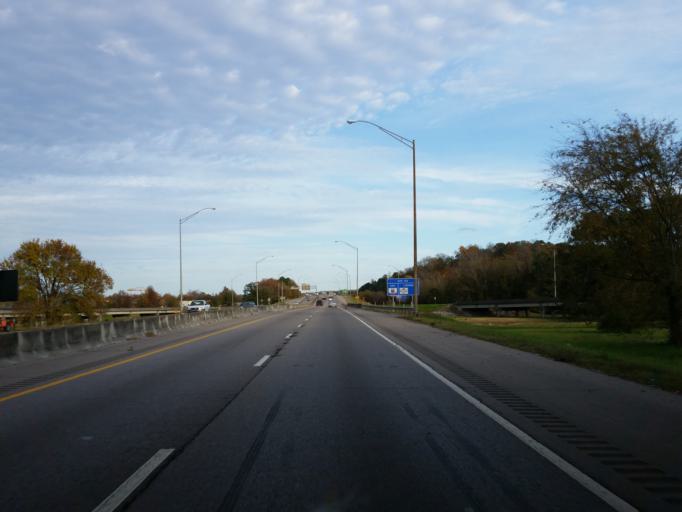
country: US
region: Mississippi
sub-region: Lauderdale County
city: Meridian
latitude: 32.3490
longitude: -88.7268
